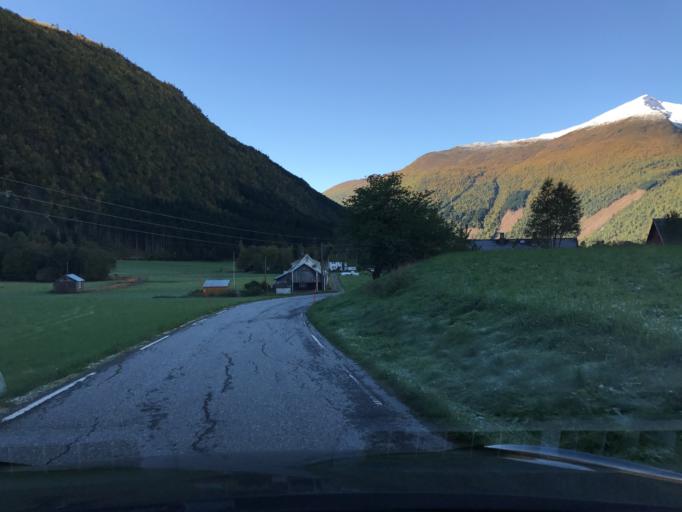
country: NO
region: More og Romsdal
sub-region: Norddal
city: Valldal
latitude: 62.3138
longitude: 7.3042
